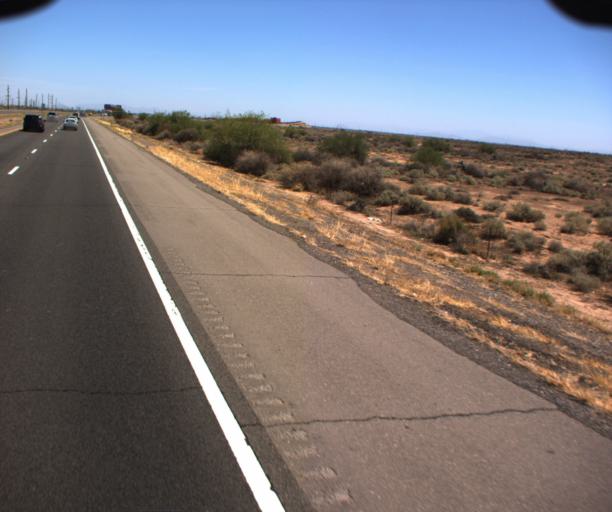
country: US
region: Arizona
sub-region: Maricopa County
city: Sun Lakes
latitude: 33.2444
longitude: -111.9804
